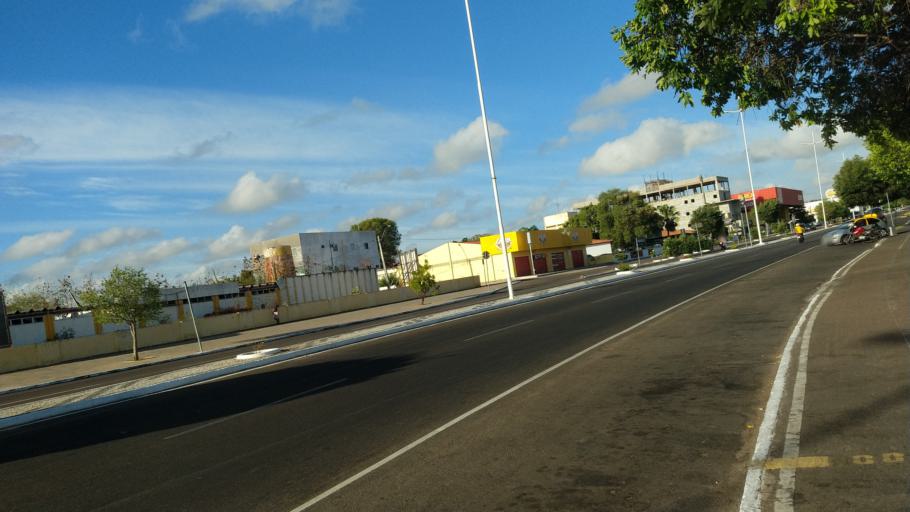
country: BR
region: Bahia
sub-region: Paulo Afonso
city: Paulo Afonso
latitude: -9.3982
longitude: -38.2213
